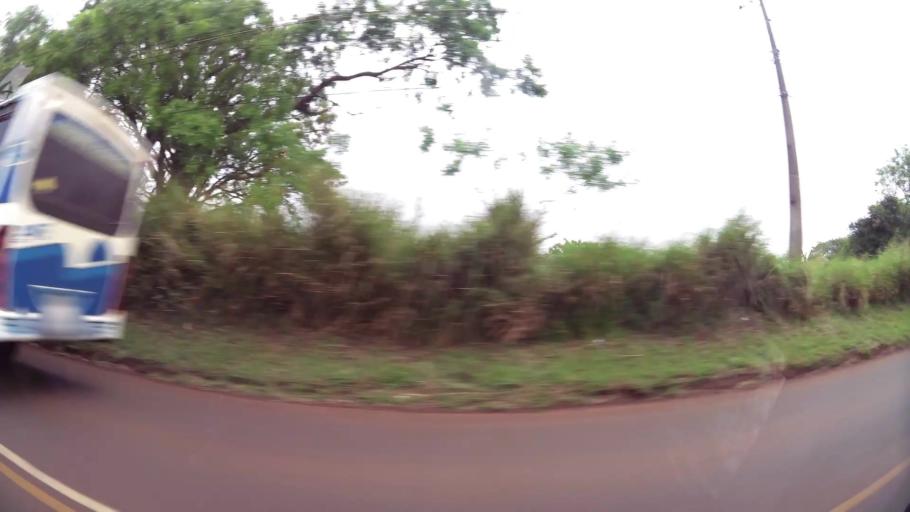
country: PY
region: Alto Parana
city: Ciudad del Este
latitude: -25.4971
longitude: -54.6734
